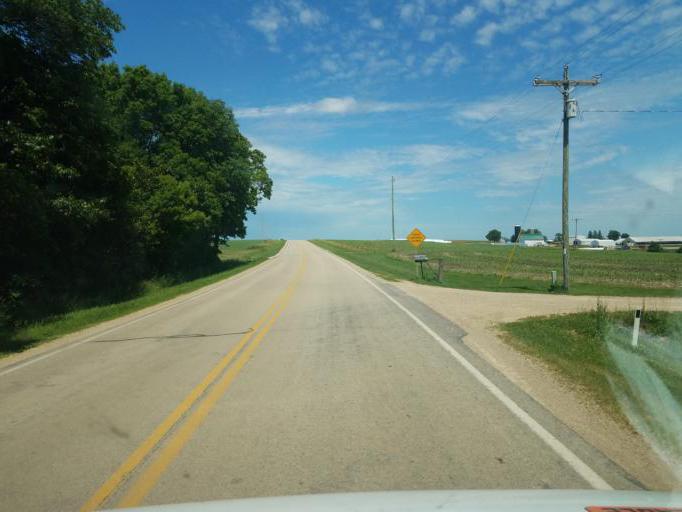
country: US
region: Wisconsin
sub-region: Vernon County
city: Hillsboro
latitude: 43.5973
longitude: -90.2902
